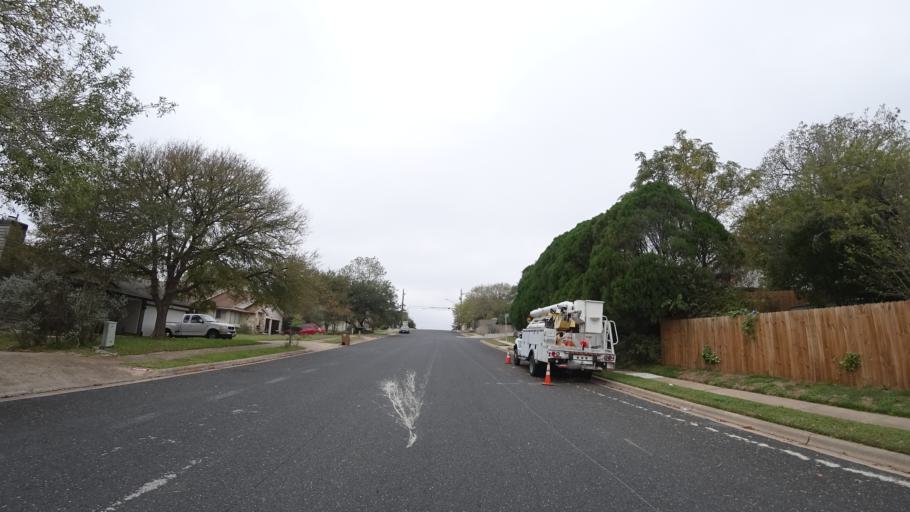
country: US
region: Texas
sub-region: Travis County
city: Barton Creek
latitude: 30.2364
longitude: -97.9003
